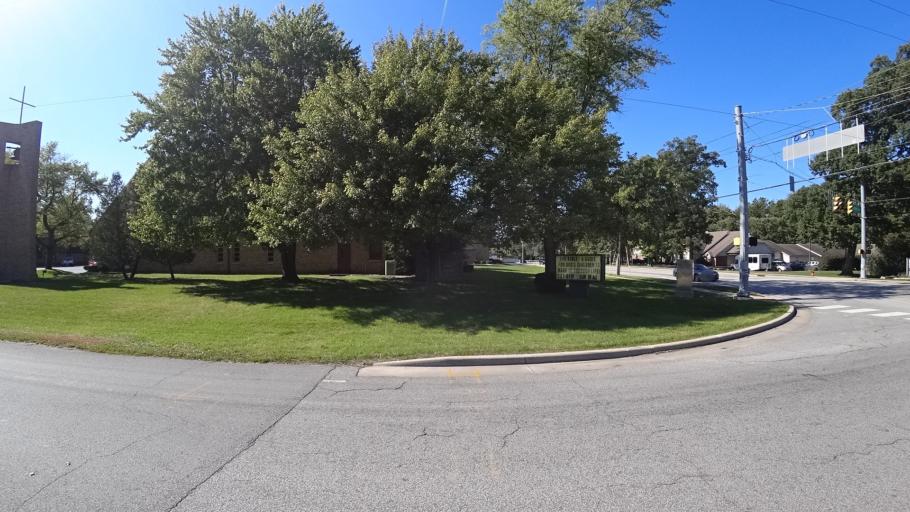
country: US
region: Indiana
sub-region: LaPorte County
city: Trail Creek
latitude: 41.6945
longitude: -86.8744
